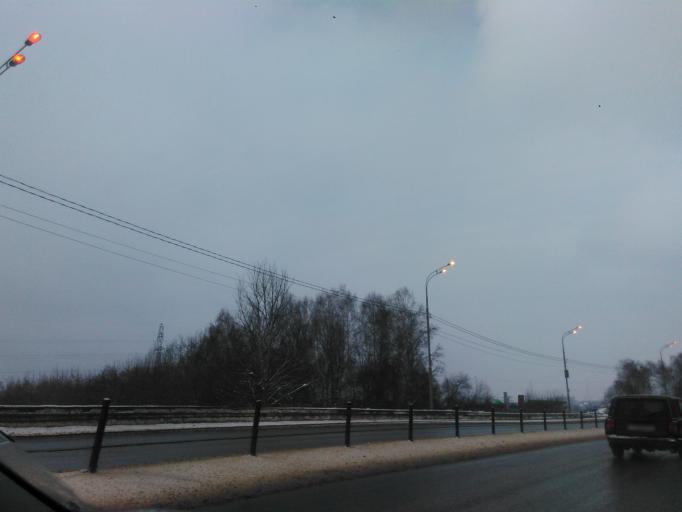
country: RU
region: Moskovskaya
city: Dedenevo
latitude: 56.2620
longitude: 37.5042
